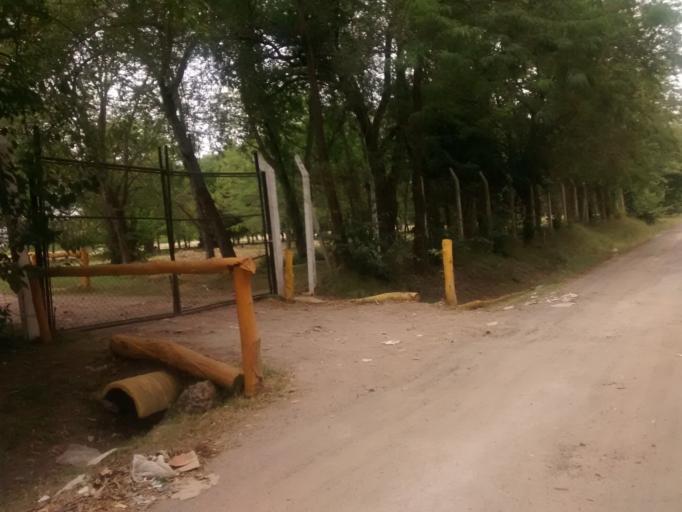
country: AR
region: Buenos Aires
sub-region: Partido de La Plata
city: La Plata
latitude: -34.8597
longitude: -58.0730
